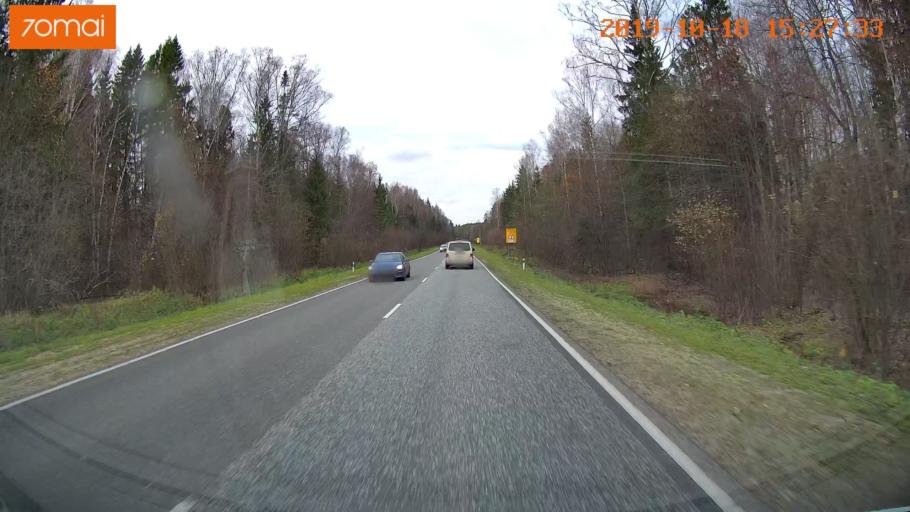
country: RU
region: Vladimir
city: Anopino
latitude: 55.7547
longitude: 40.6714
